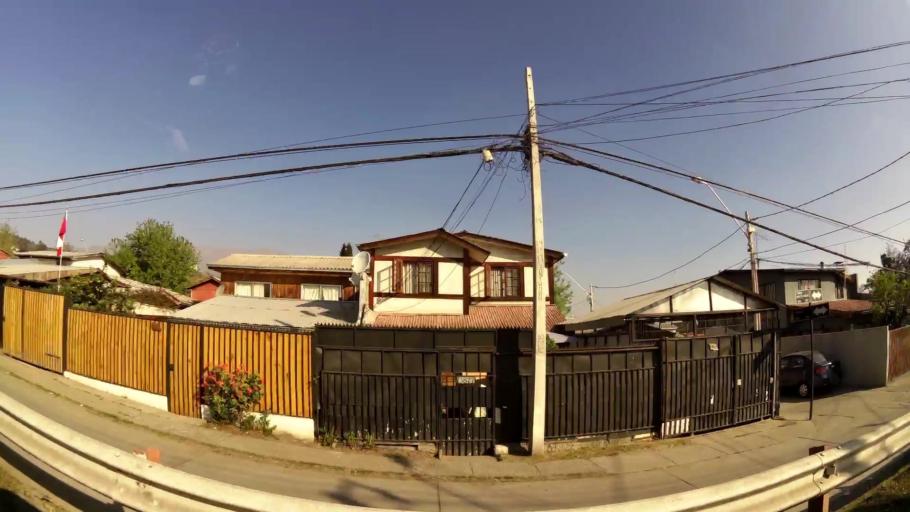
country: CL
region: Santiago Metropolitan
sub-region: Provincia de Santiago
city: Villa Presidente Frei, Nunoa, Santiago, Chile
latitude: -33.3542
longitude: -70.5070
